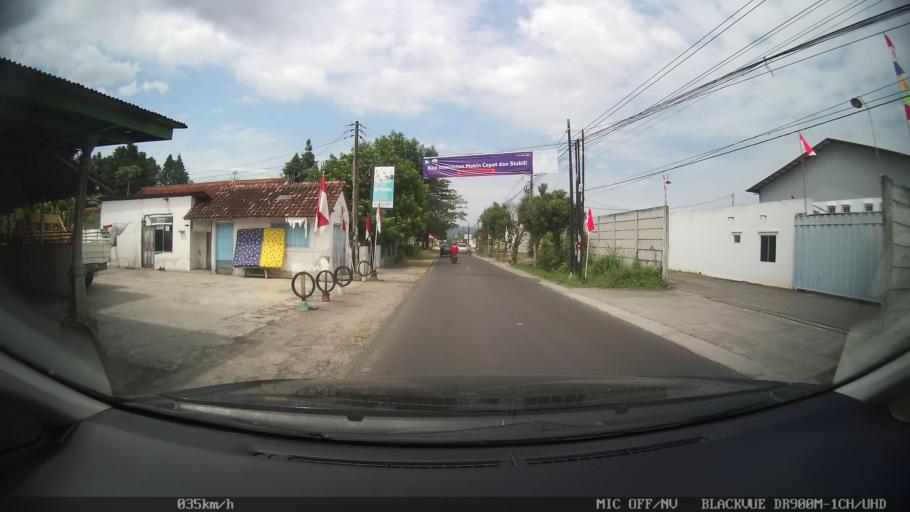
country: ID
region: Daerah Istimewa Yogyakarta
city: Depok
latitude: -7.8103
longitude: 110.4431
